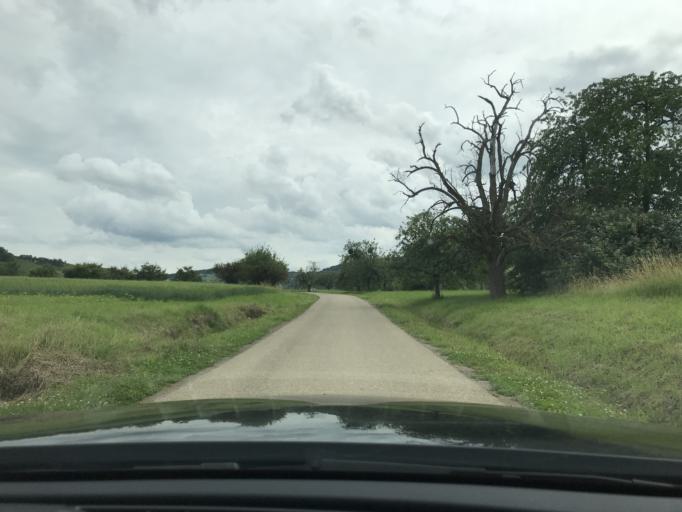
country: DE
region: Baden-Wuerttemberg
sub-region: Regierungsbezirk Stuttgart
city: Weinstadt-Endersbach
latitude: 48.8007
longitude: 9.3604
